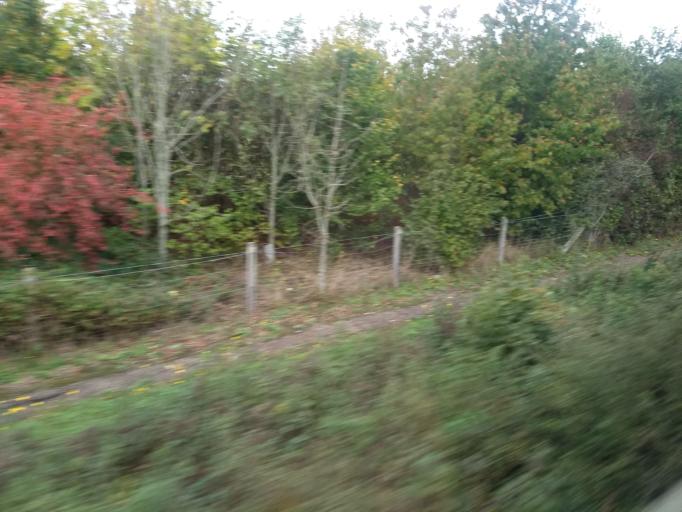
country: GB
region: England
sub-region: Isle of Wight
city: Ryde
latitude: 50.7276
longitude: -1.2010
